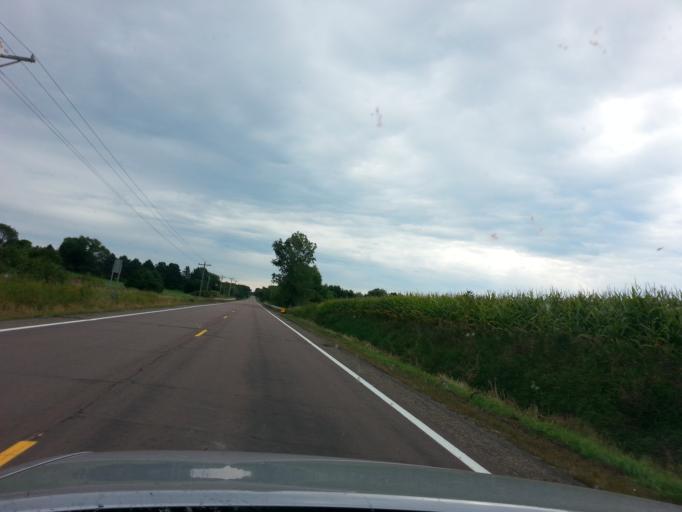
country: US
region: Minnesota
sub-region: Dakota County
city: Farmington
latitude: 44.6304
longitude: -93.0535
